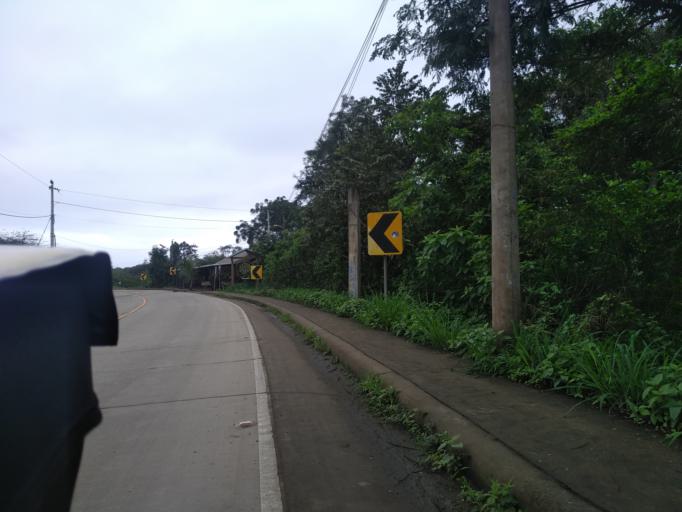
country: EC
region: Manabi
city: Jipijapa
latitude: -1.6745
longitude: -80.8111
